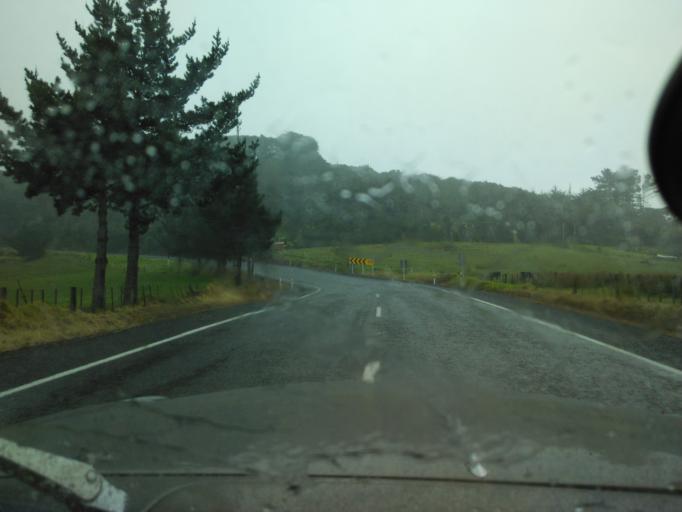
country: NZ
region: Auckland
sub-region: Auckland
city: Wellsford
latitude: -36.4324
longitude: 174.4372
